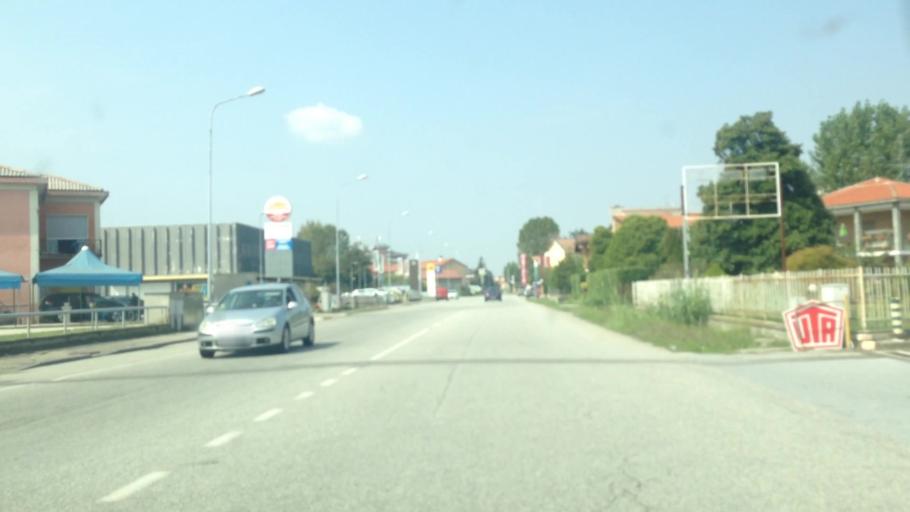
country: IT
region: Piedmont
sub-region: Provincia di Alessandria
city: Casale Monferrato
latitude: 45.1295
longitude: 8.4753
